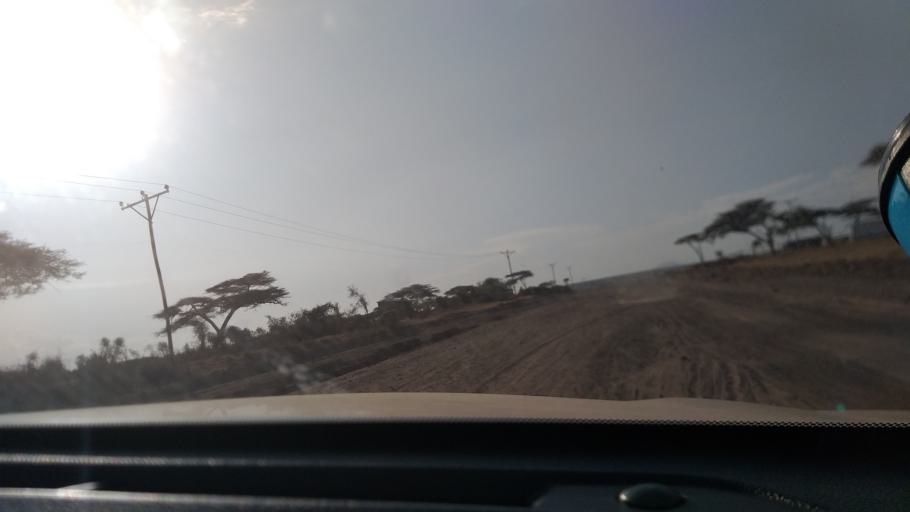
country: ET
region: Oromiya
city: Shashemene
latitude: 7.4980
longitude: 38.6984
